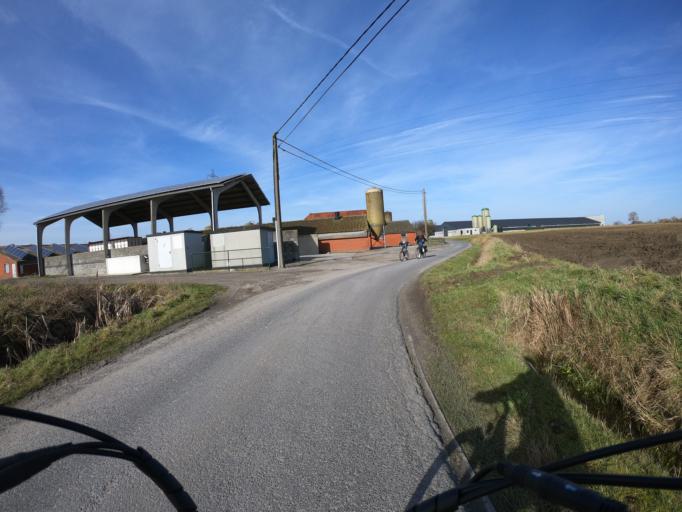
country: BE
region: Flanders
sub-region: Provincie West-Vlaanderen
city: Menen
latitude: 50.8191
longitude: 3.1278
